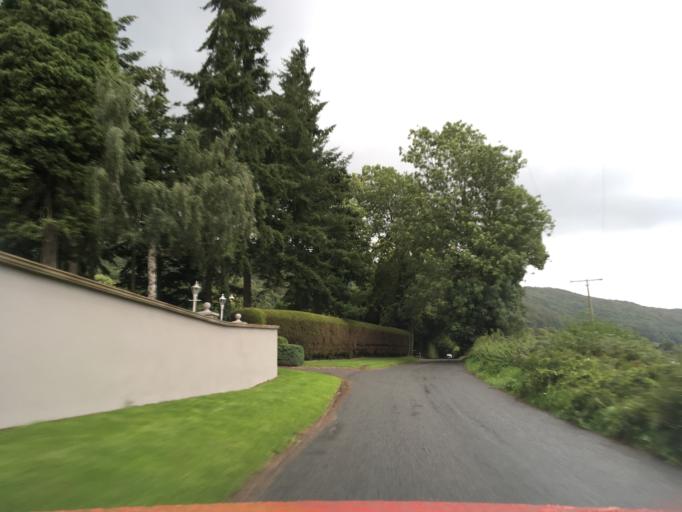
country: GB
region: Wales
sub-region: Monmouthshire
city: Llangybi
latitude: 51.6473
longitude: -2.8823
